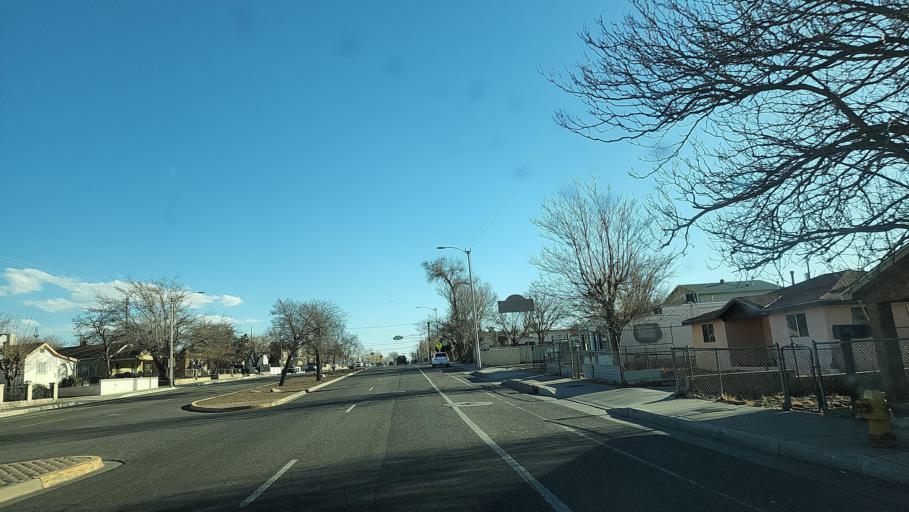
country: US
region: New Mexico
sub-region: Bernalillo County
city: Albuquerque
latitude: 35.0642
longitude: -106.6455
